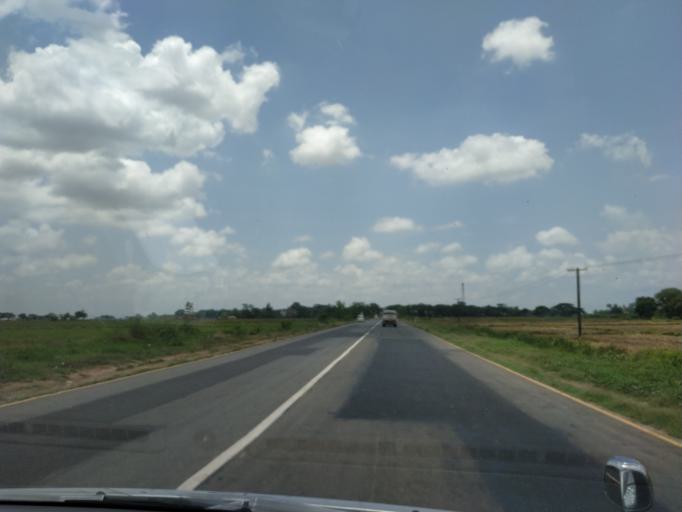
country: MM
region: Bago
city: Bago
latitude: 17.4679
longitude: 96.5746
